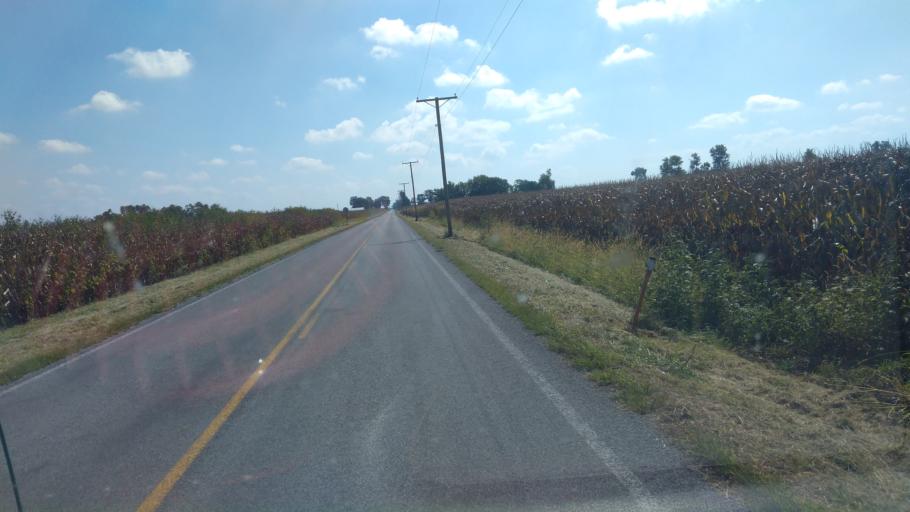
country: US
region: Ohio
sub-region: Hardin County
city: Ada
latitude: 40.7735
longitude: -83.7849
